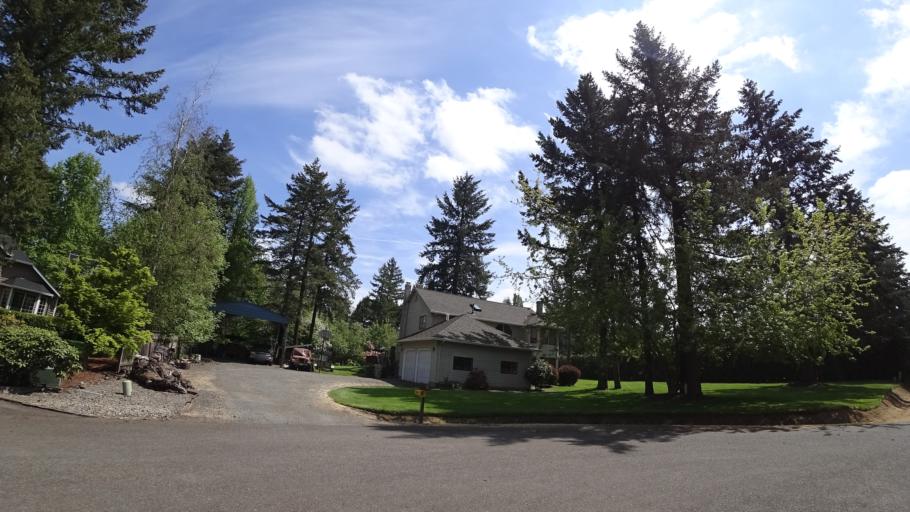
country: US
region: Oregon
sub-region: Washington County
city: Aloha
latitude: 45.4721
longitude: -122.8962
